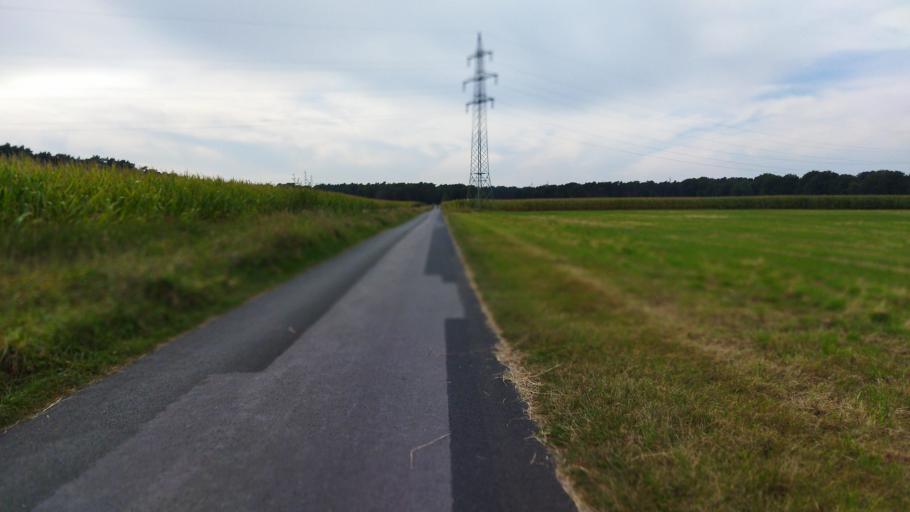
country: DE
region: Lower Saxony
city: Bad Laer
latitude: 52.1017
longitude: 8.0540
